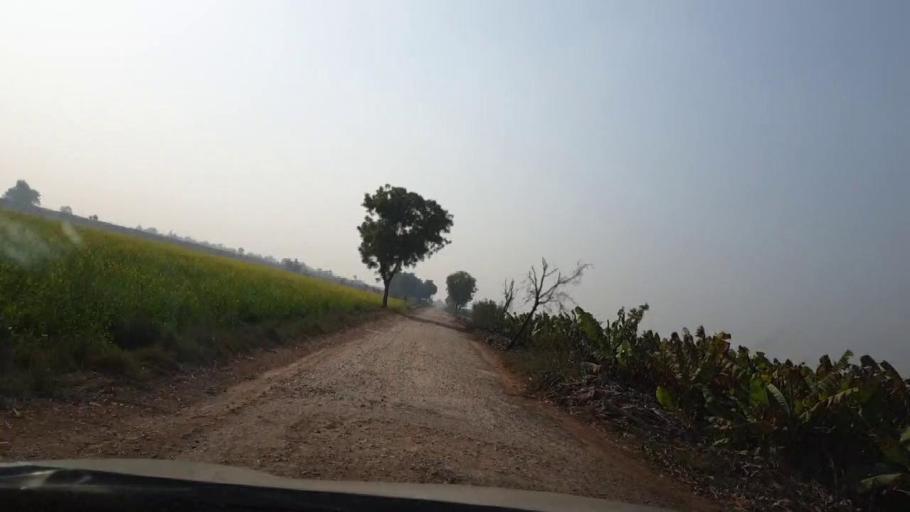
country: PK
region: Sindh
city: Matiari
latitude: 25.6837
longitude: 68.5240
